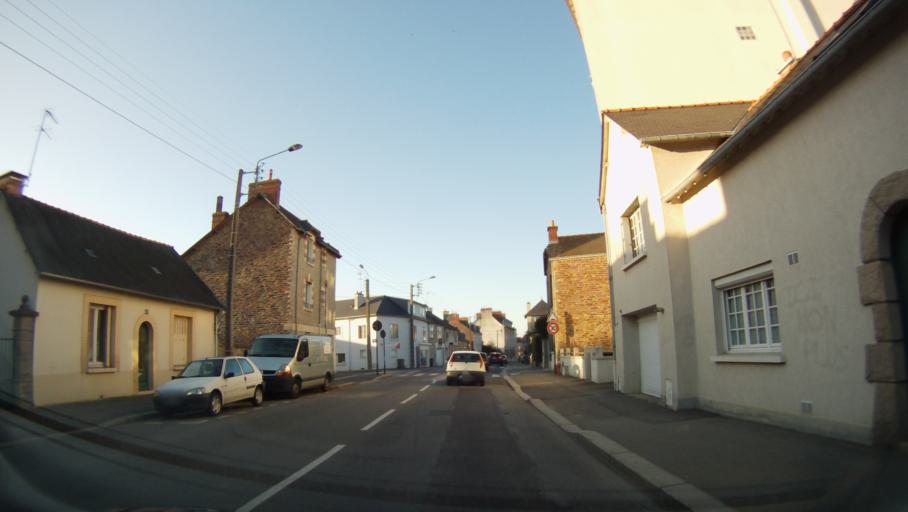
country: FR
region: Brittany
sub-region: Departement d'Ille-et-Vilaine
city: Rennes
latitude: 48.0961
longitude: -1.6716
